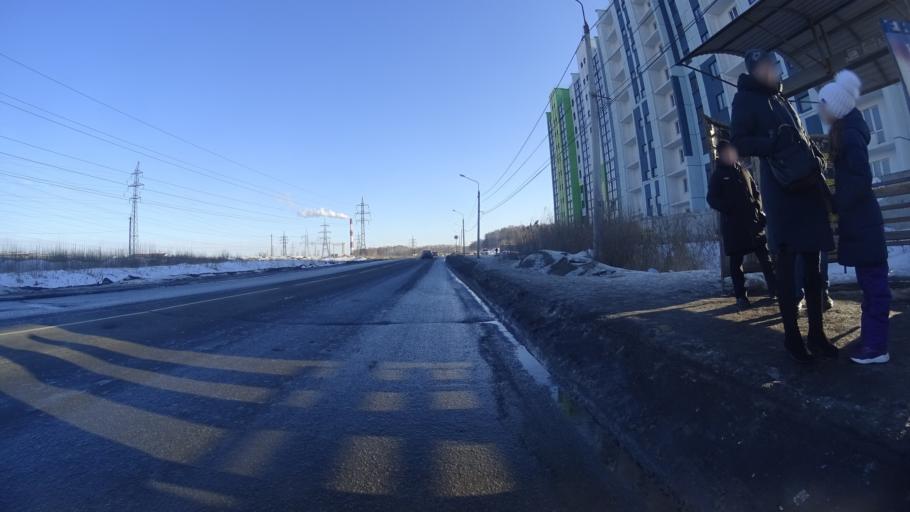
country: RU
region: Chelyabinsk
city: Roshchino
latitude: 55.2144
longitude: 61.3049
